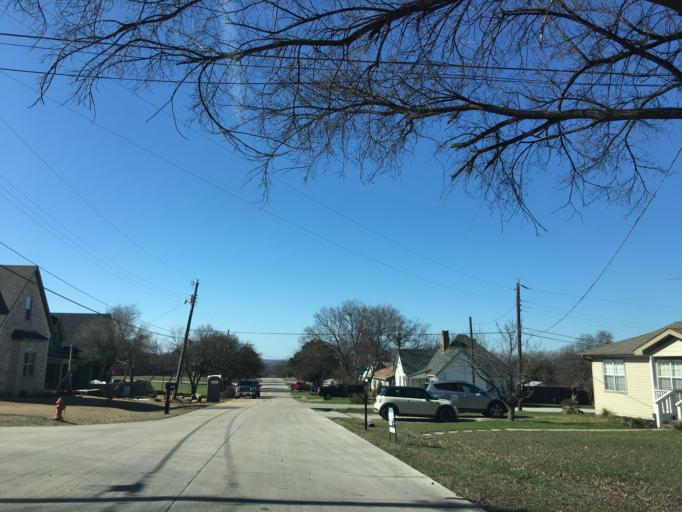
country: US
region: Texas
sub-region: Collin County
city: Prosper
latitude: 33.2351
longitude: -96.7956
